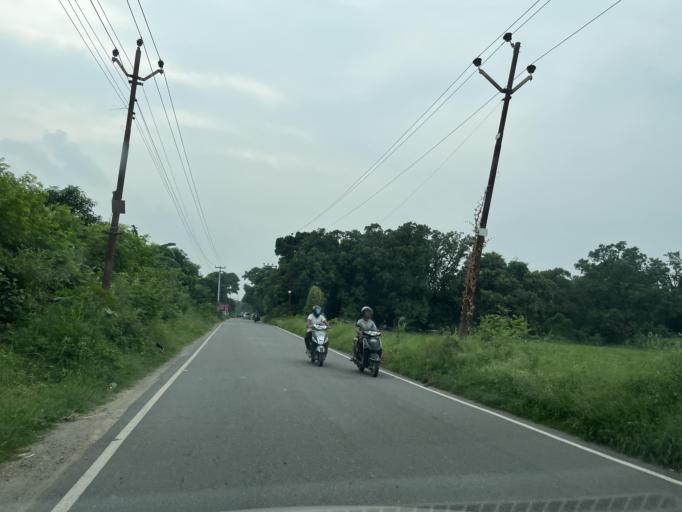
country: IN
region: Uttarakhand
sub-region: Naini Tal
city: Haldwani
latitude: 29.1733
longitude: 79.4799
